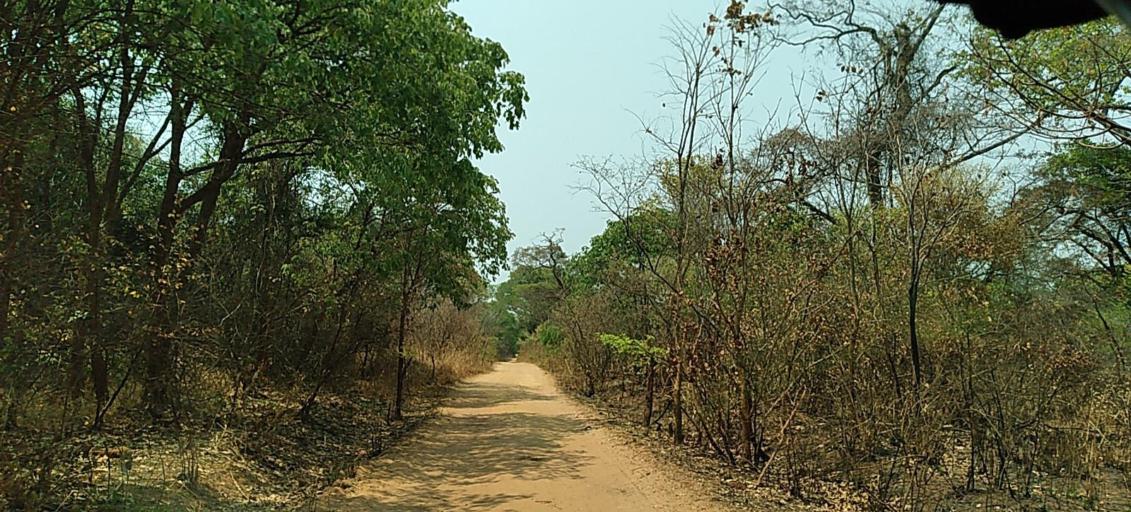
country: ZM
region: North-Western
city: Kabompo
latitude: -13.7062
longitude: 24.3229
